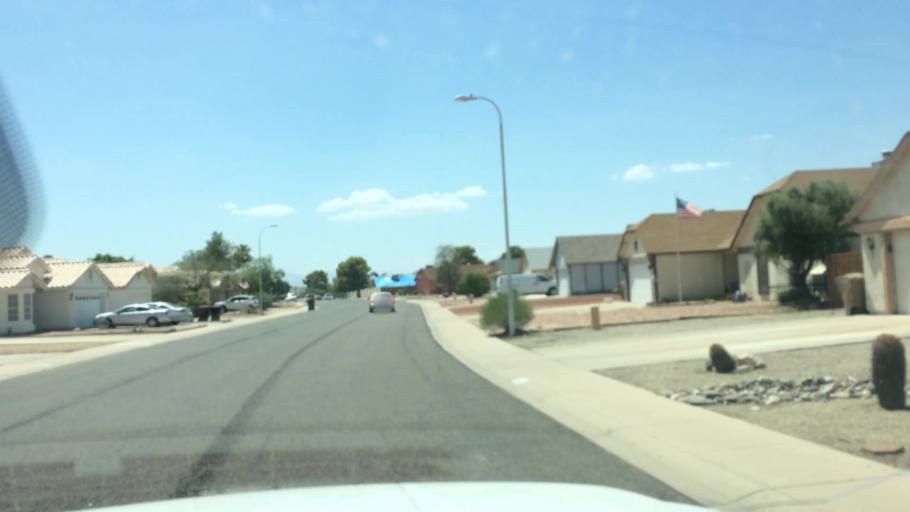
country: US
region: Arizona
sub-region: Maricopa County
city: Peoria
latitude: 33.5984
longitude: -112.2403
